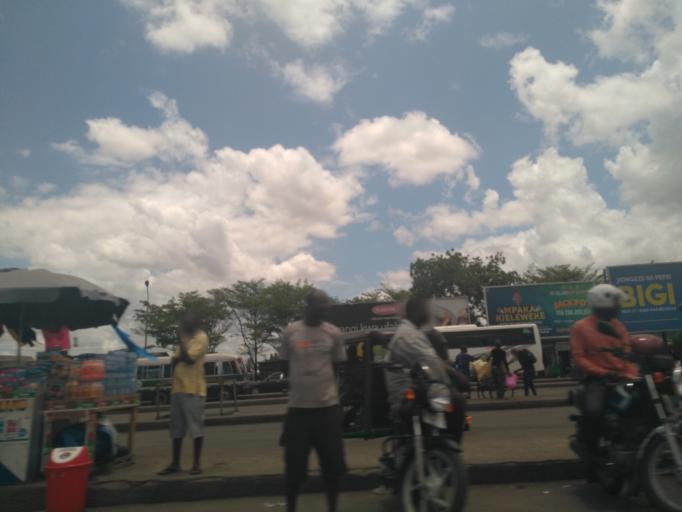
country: TZ
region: Dar es Salaam
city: Dar es Salaam
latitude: -6.8647
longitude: 39.2660
